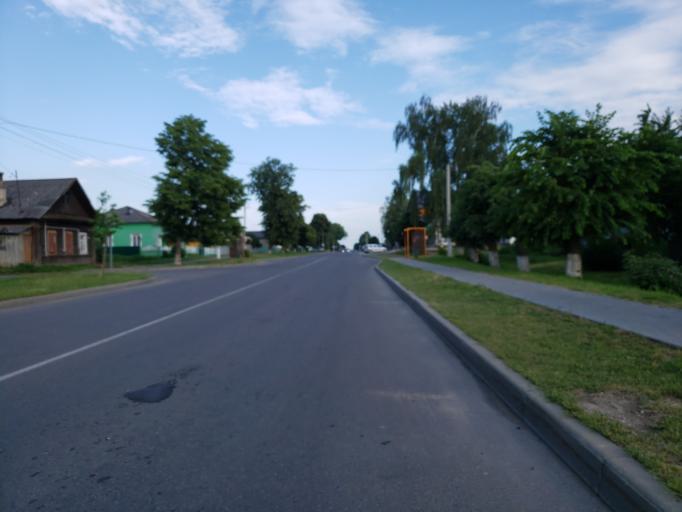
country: BY
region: Minsk
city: Chervyen'
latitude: 53.7065
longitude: 28.4334
